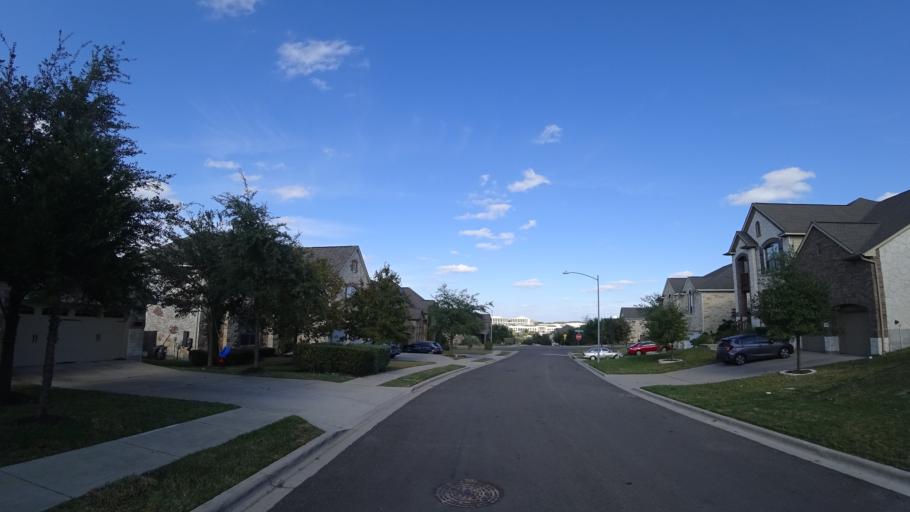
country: US
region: Texas
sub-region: Travis County
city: Barton Creek
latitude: 30.2490
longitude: -97.8778
